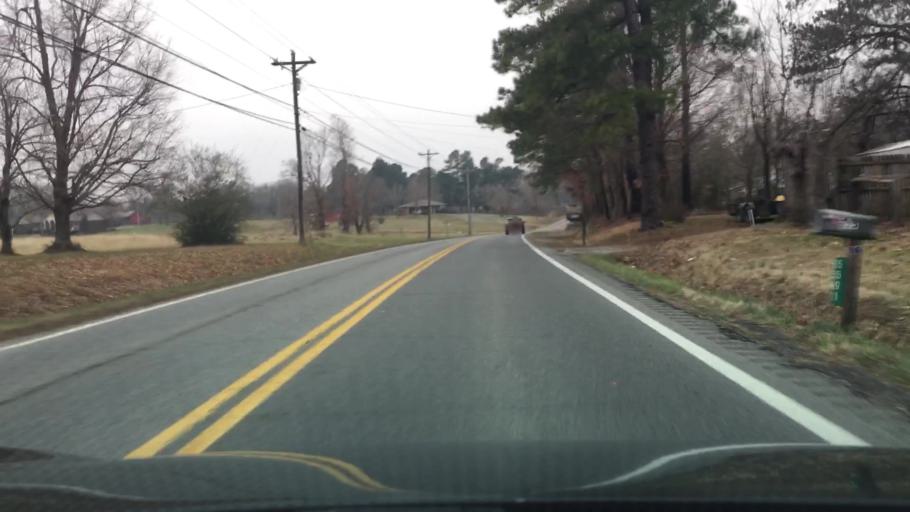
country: US
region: Kentucky
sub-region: Marshall County
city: Calvert City
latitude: 36.9699
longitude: -88.4186
